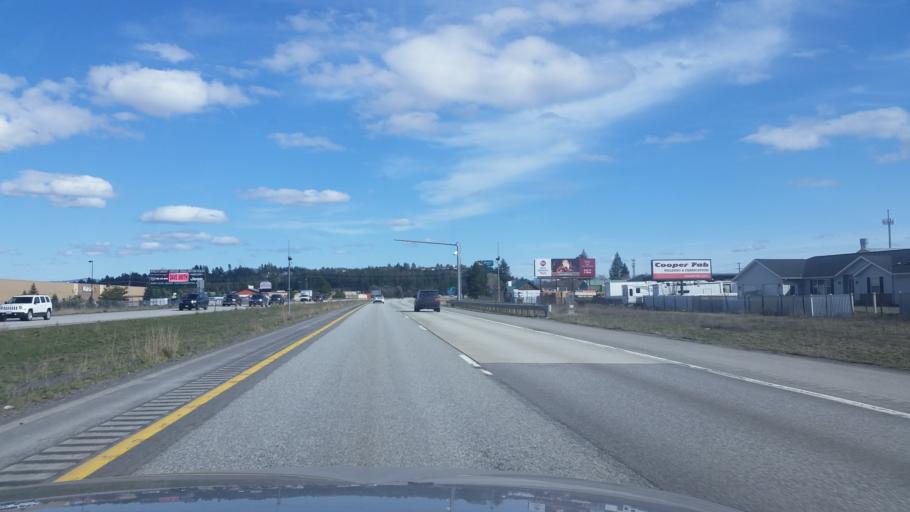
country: US
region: Idaho
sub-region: Kootenai County
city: Post Falls
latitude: 47.7125
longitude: -116.9103
